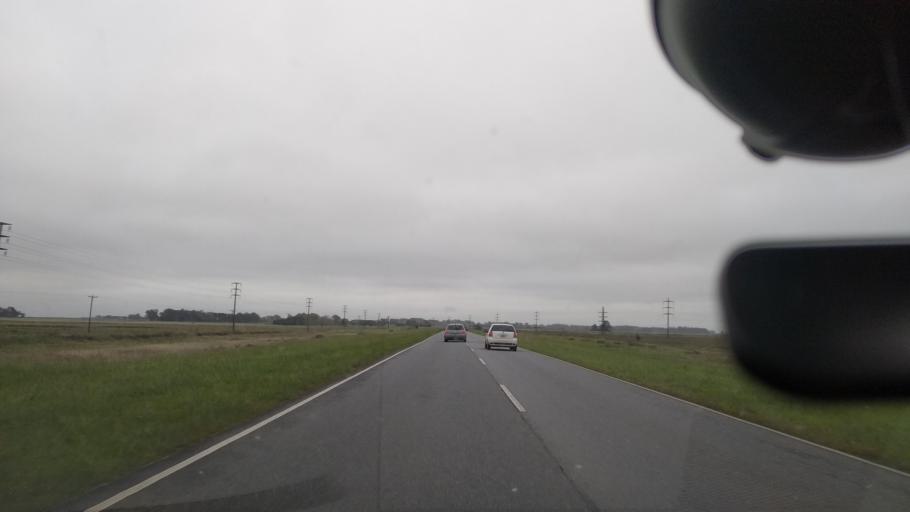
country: AR
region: Buenos Aires
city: Veronica
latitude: -35.3579
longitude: -57.4060
